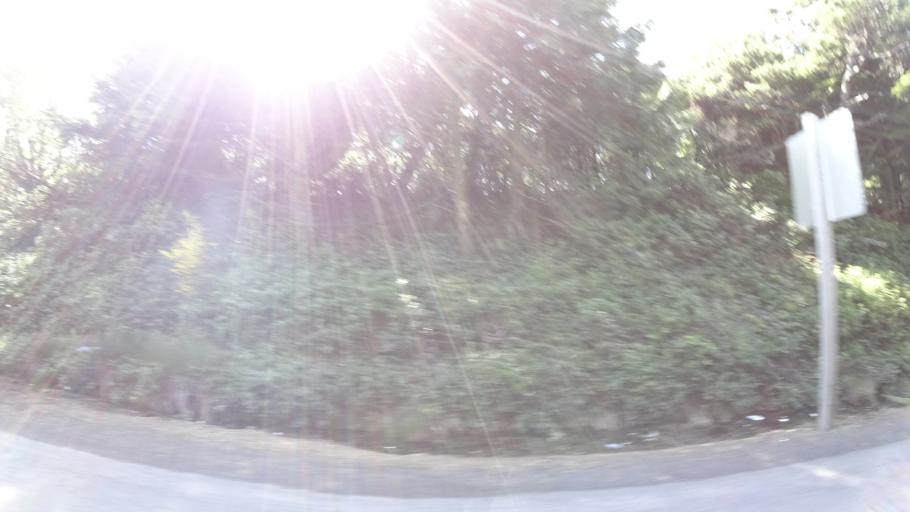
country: US
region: Oregon
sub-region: Lincoln County
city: Newport
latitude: 44.6842
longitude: -124.0635
